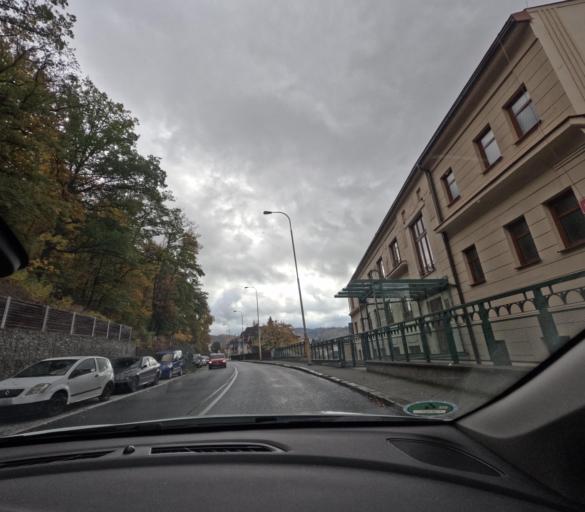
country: CZ
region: Karlovarsky
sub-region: Okres Karlovy Vary
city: Karlovy Vary
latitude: 50.2278
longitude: 12.8821
